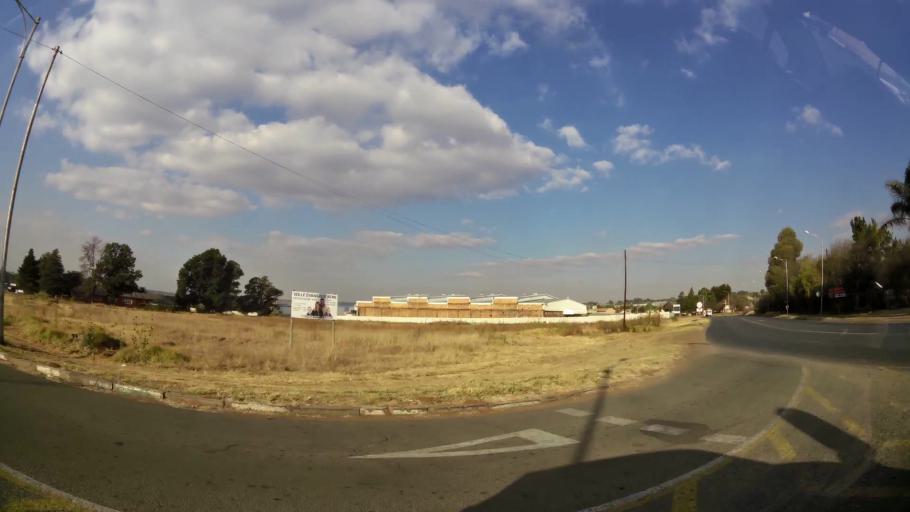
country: ZA
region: Gauteng
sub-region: West Rand District Municipality
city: Krugersdorp
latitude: -26.1015
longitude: 27.7390
